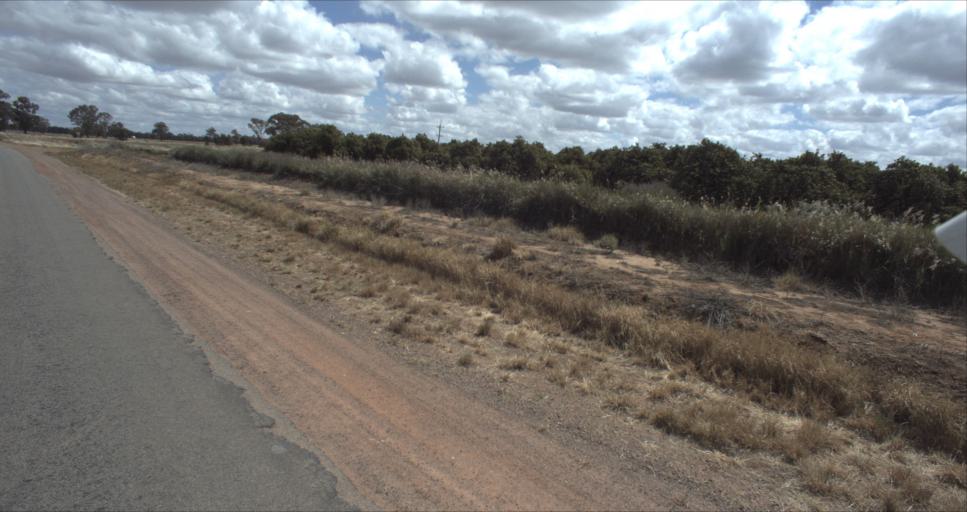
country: AU
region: New South Wales
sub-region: Leeton
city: Leeton
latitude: -34.5891
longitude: 146.3702
